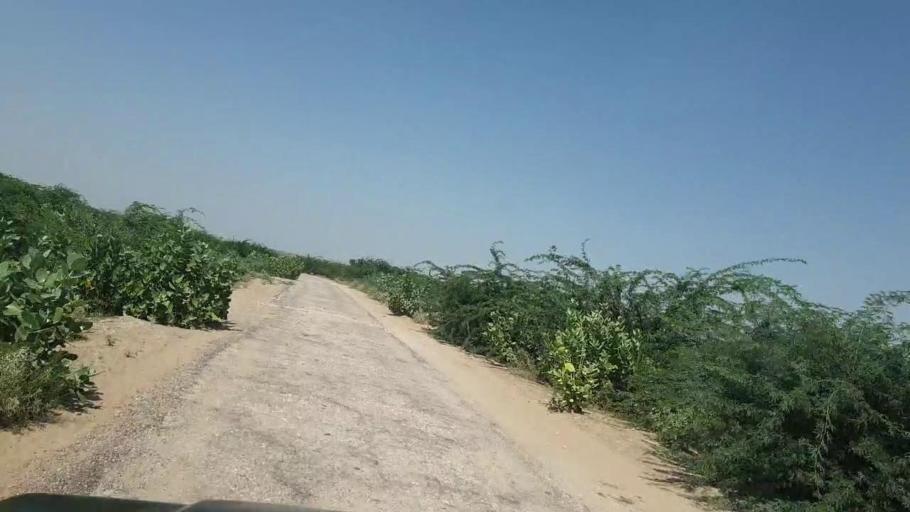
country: PK
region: Sindh
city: Chor
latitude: 25.4020
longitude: 70.3104
